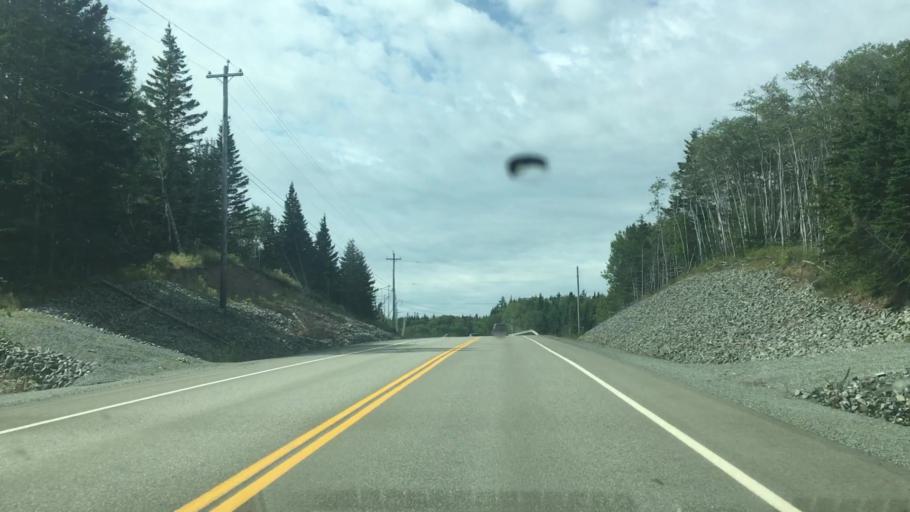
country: CA
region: Nova Scotia
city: Princeville
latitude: 45.6758
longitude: -60.7901
